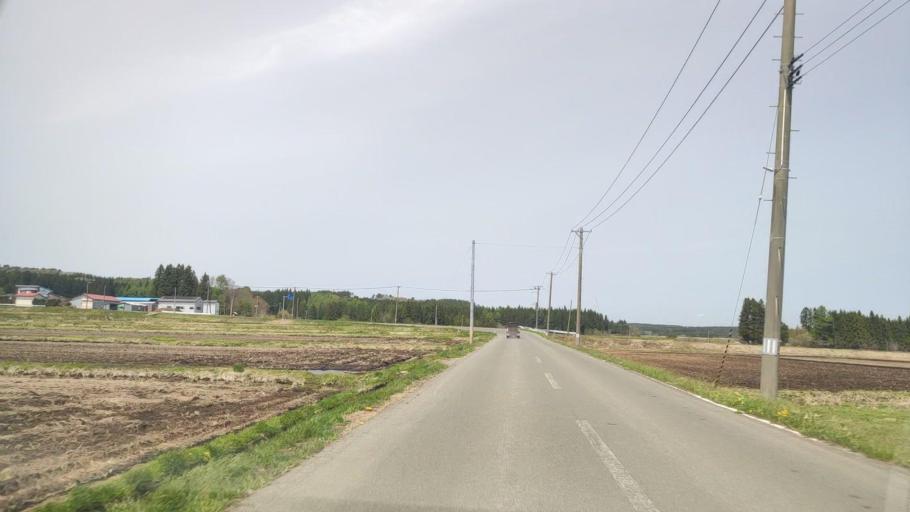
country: JP
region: Aomori
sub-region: Misawa Shi
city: Inuotose
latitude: 40.7621
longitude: 141.1198
